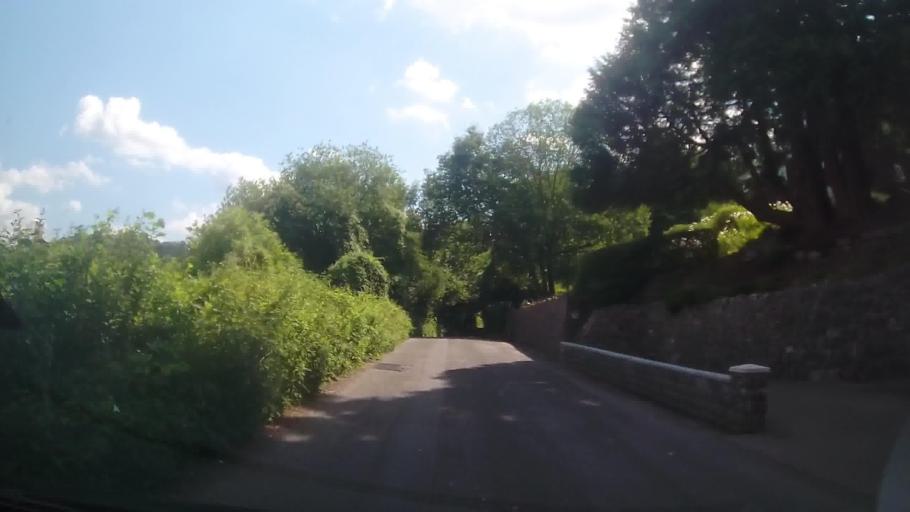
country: GB
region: England
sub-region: Herefordshire
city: Whitchurch
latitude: 51.8512
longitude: -2.6499
